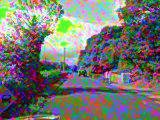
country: IE
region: Ulster
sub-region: County Donegal
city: Letterkenny
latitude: 55.0211
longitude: -7.7896
